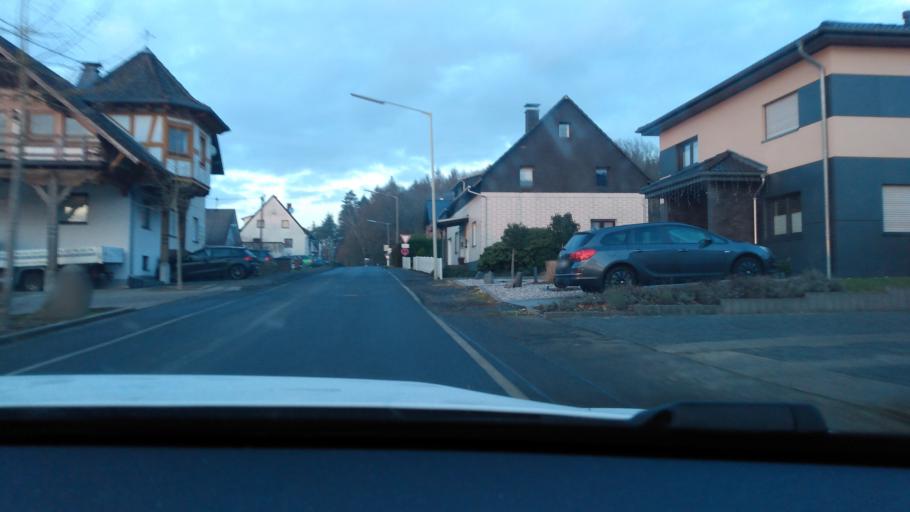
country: DE
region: Rheinland-Pfalz
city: Kircheib
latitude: 50.7066
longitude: 7.4683
